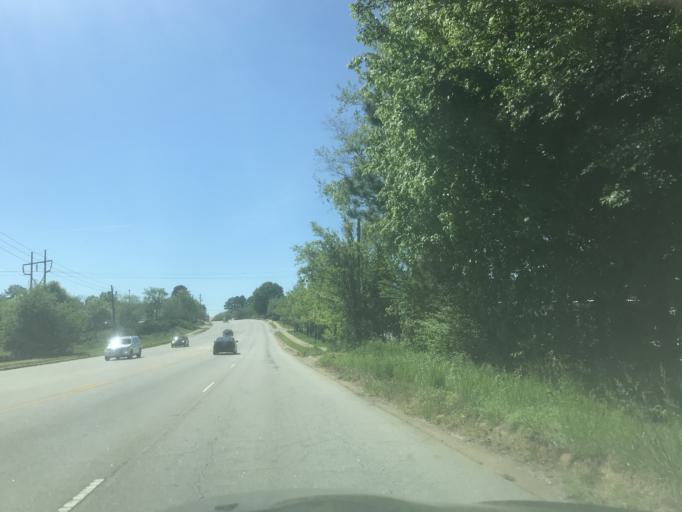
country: US
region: North Carolina
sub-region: Wake County
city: Garner
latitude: 35.7313
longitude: -78.6433
